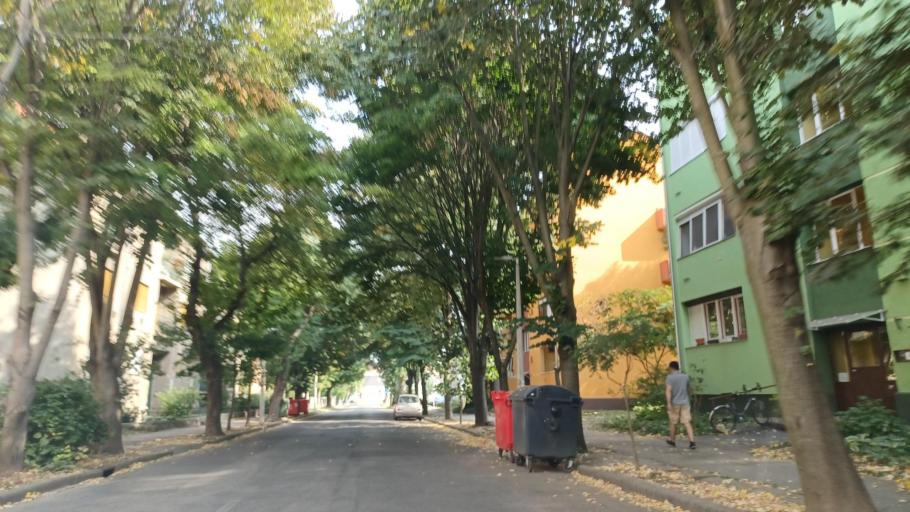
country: HU
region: Baranya
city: Pecs
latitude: 46.0679
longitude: 18.2207
